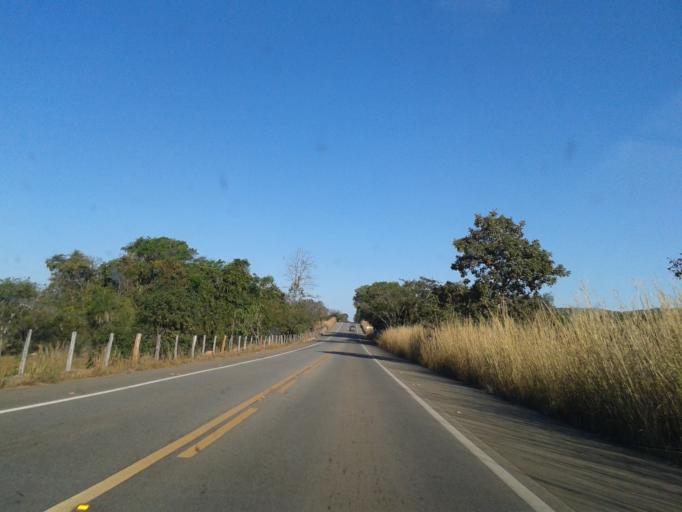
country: BR
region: Goias
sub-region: Itapuranga
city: Itapuranga
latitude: -15.5707
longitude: -50.2778
